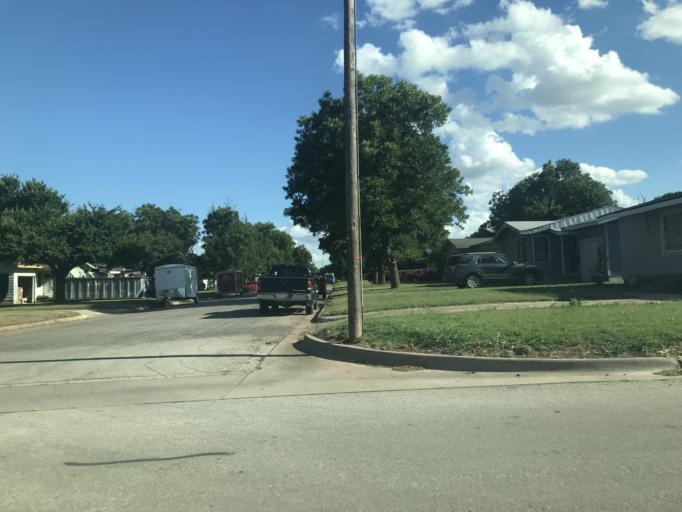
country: US
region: Texas
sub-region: Taylor County
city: Abilene
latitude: 32.4360
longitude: -99.7835
